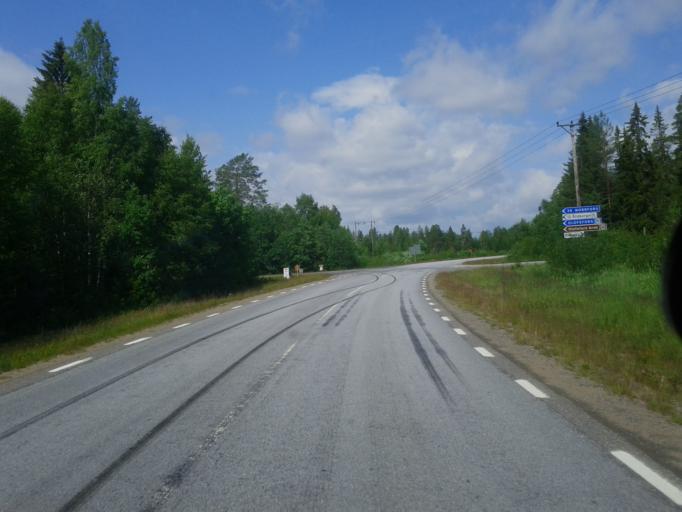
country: SE
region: Vaesterbotten
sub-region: Nordmalings Kommun
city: Nordmaling
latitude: 63.5833
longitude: 19.4526
